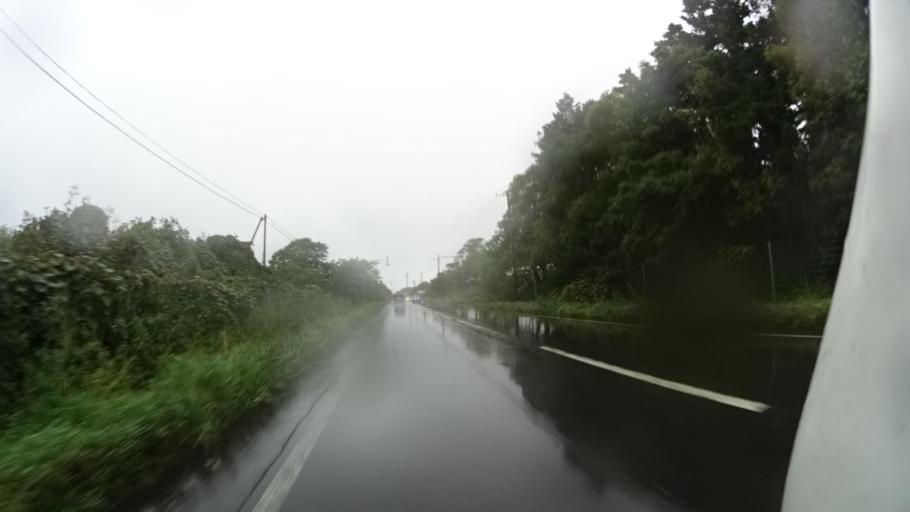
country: JP
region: Hokkaido
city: Nemuro
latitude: 43.2603
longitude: 145.4271
